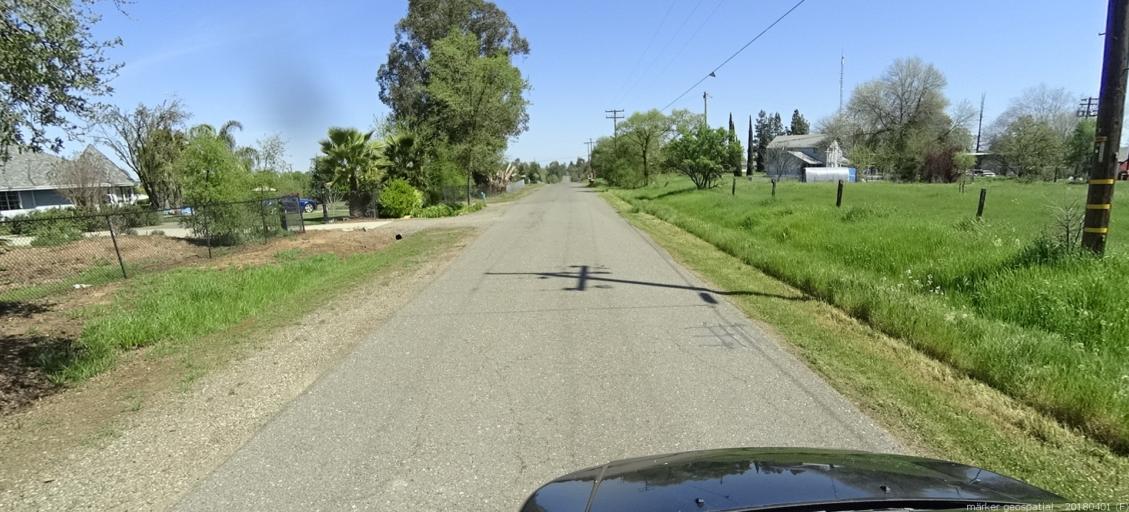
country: US
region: California
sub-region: Sacramento County
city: Wilton
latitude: 38.3941
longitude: -121.2257
